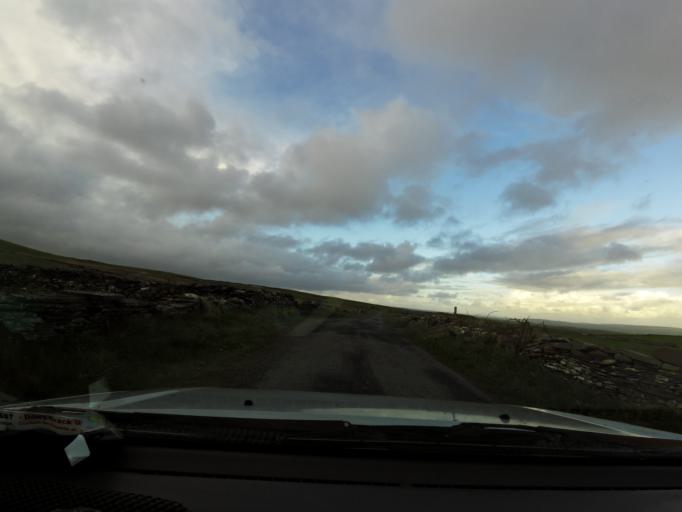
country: IE
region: Munster
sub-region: An Clar
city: Kilrush
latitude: 52.9591
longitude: -9.4336
